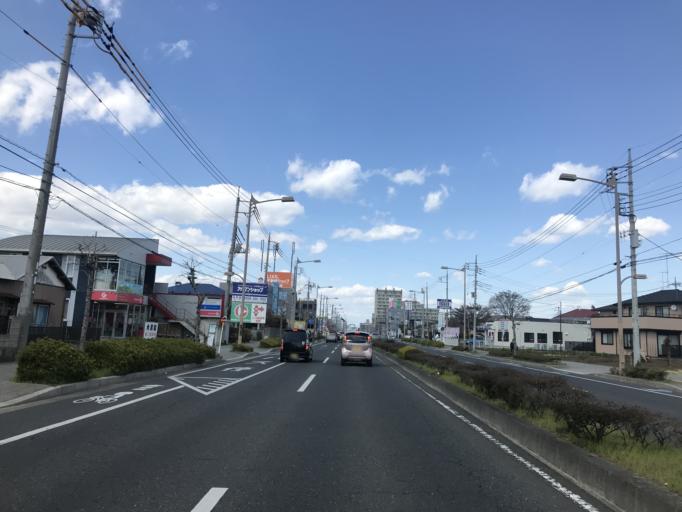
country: JP
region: Ibaraki
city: Mito-shi
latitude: 36.3563
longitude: 140.4734
